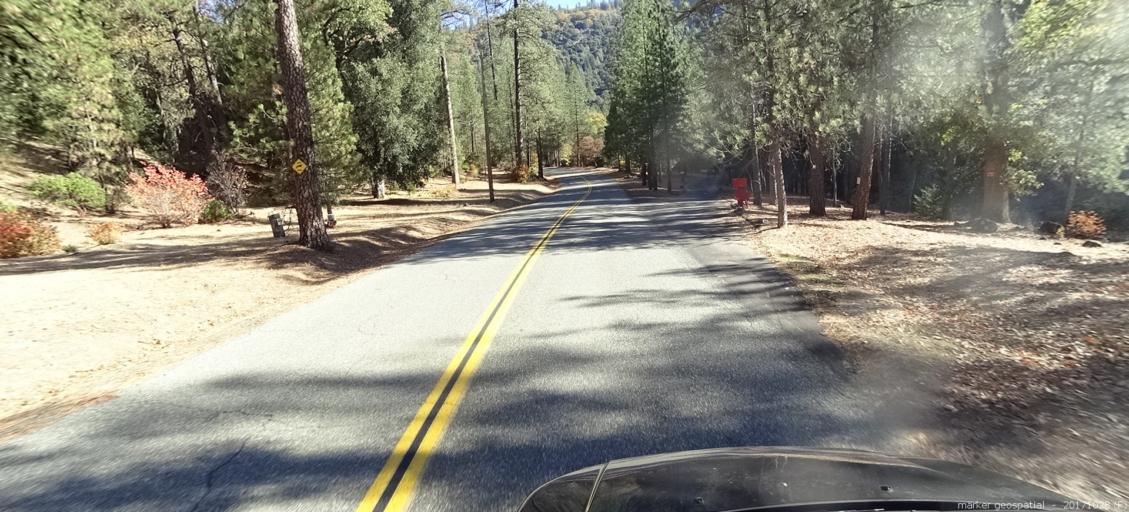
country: US
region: California
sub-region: Trinity County
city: Lewiston
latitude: 40.7845
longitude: -122.6125
